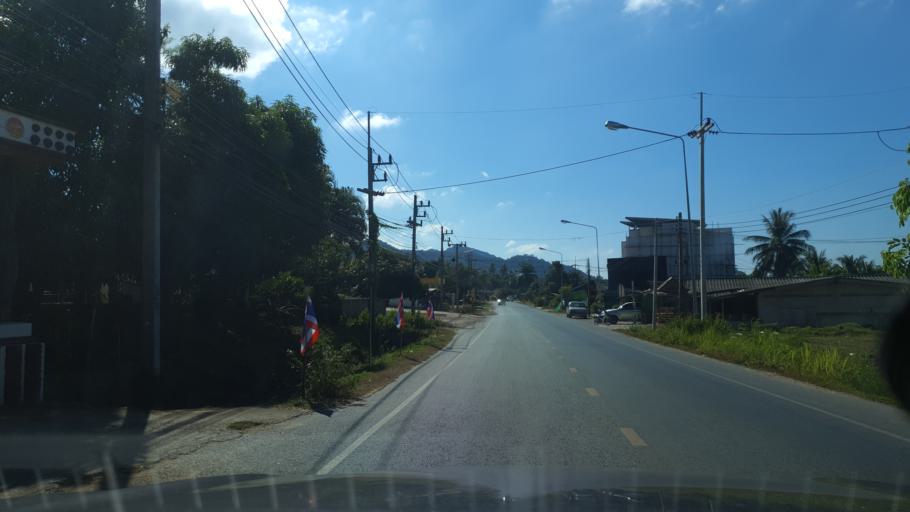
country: TH
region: Phangnga
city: Ban Ao Nang
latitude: 8.0605
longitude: 98.8136
